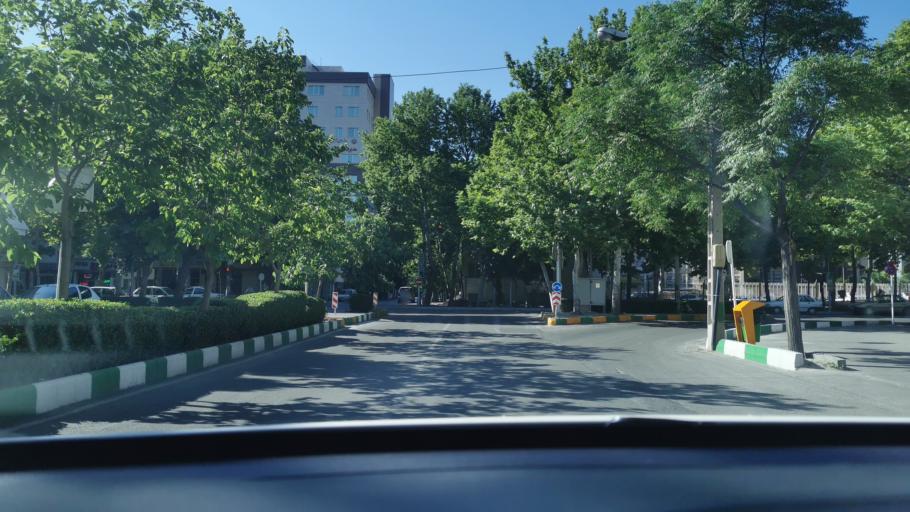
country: IR
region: Razavi Khorasan
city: Mashhad
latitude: 36.2873
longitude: 59.5738
